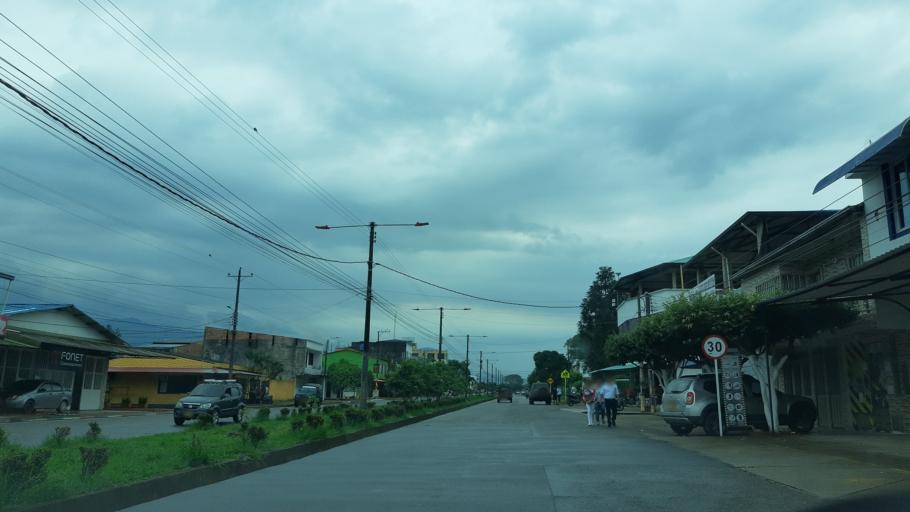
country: CO
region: Casanare
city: Monterrey
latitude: 4.8815
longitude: -72.8948
